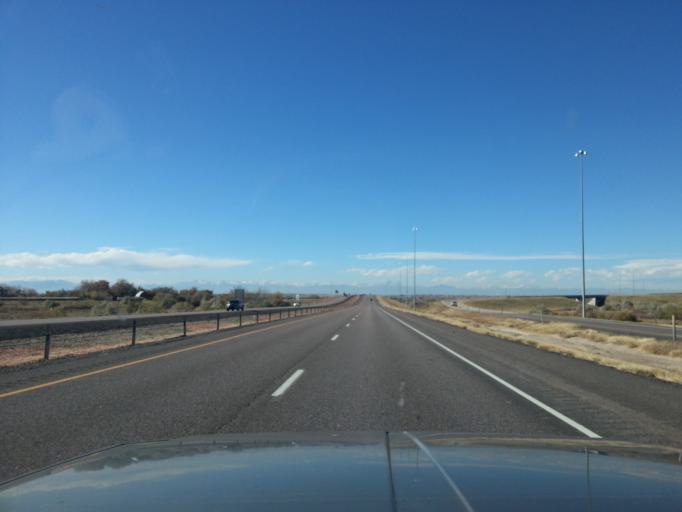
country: US
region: Colorado
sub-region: Adams County
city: Brighton
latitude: 39.9214
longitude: -104.7941
